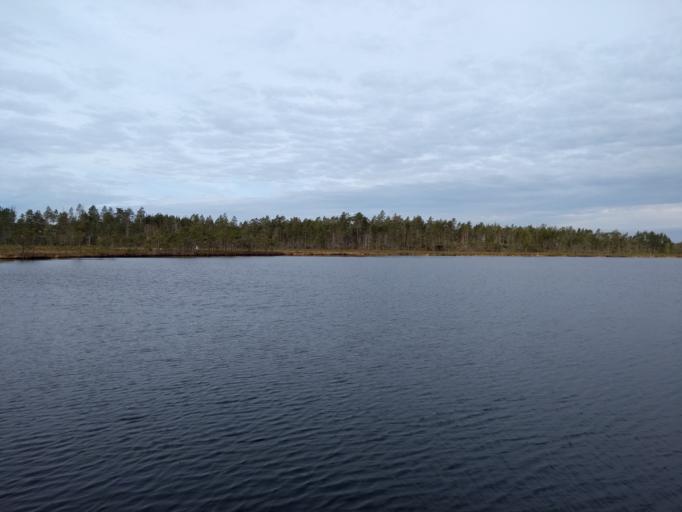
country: SE
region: Soedermanland
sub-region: Nykopings Kommun
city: Olstorp
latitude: 58.7000
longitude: 16.5441
